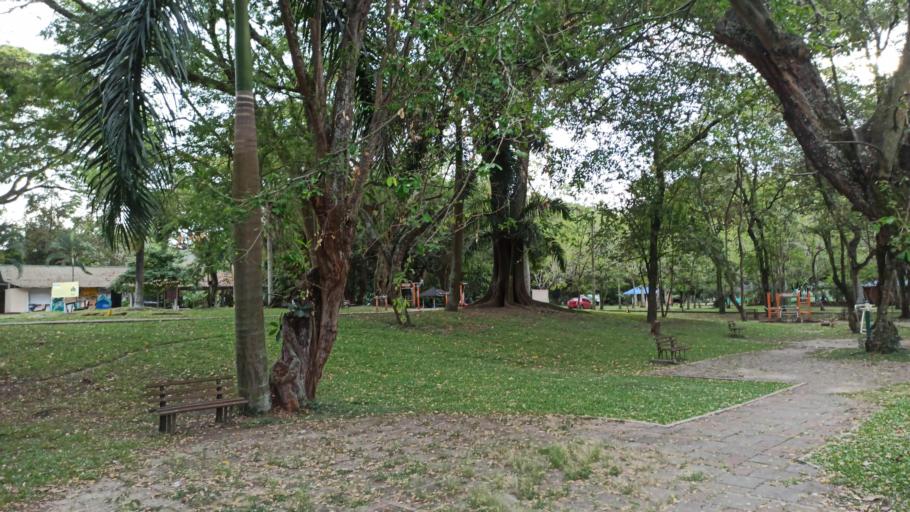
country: CO
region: Valle del Cauca
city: Palmira
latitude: 3.5289
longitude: -76.2845
